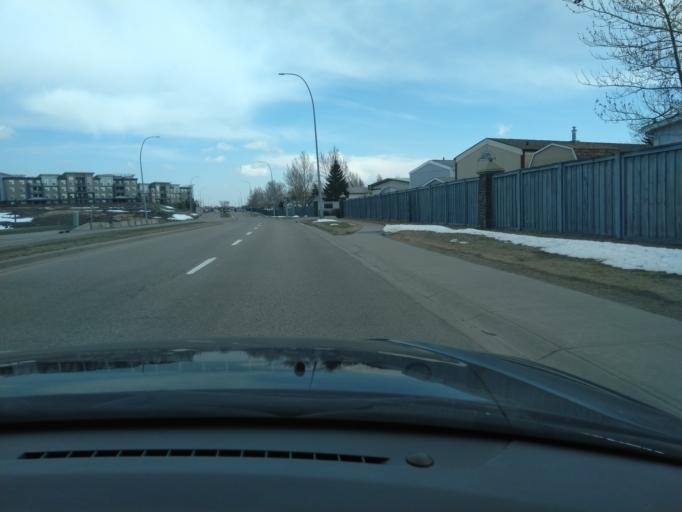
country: CA
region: Alberta
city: Calgary
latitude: 51.1289
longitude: -114.2147
